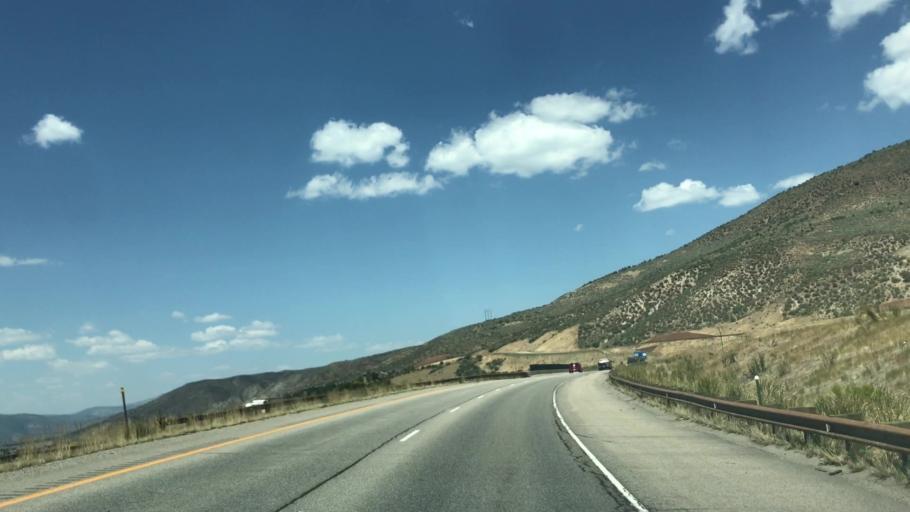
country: US
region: Colorado
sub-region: Eagle County
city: Avon
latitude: 39.6263
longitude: -106.4940
